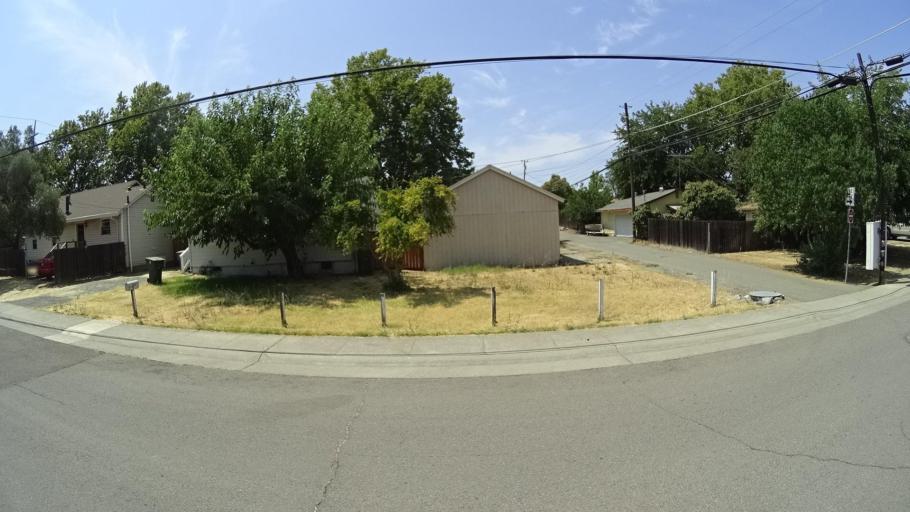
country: US
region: California
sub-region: Placer County
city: Rocklin
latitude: 38.7918
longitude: -121.2311
